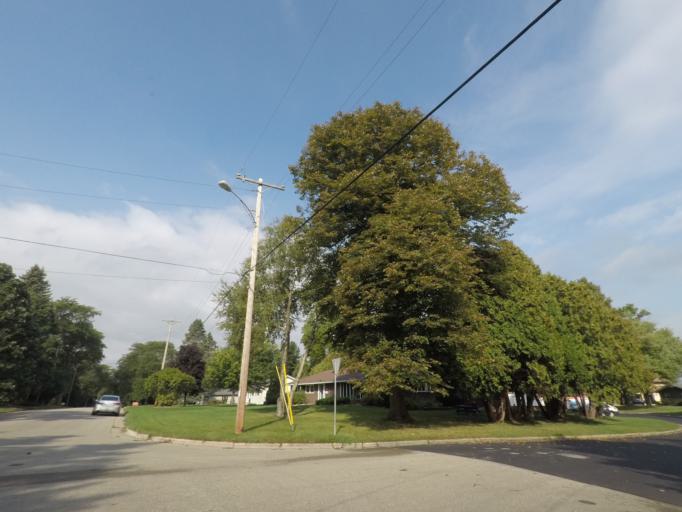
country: US
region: Wisconsin
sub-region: Dane County
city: Shorewood Hills
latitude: 43.0410
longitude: -89.4652
